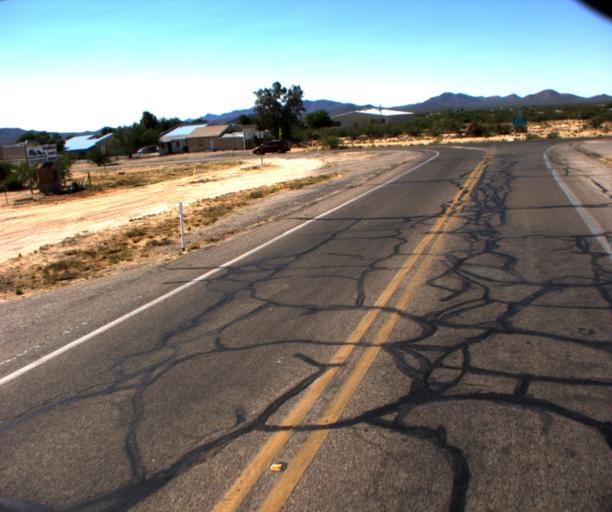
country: US
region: Arizona
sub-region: Pima County
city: Three Points
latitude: 32.0760
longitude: -111.3133
